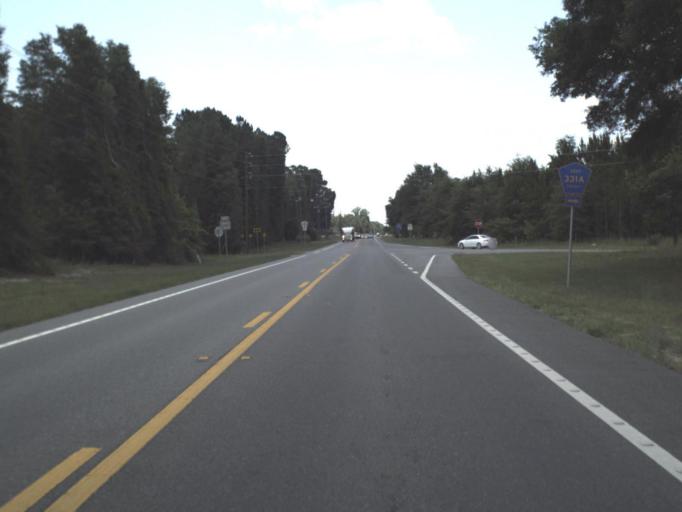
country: US
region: Florida
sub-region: Levy County
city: Williston
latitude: 29.4141
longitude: -82.4307
